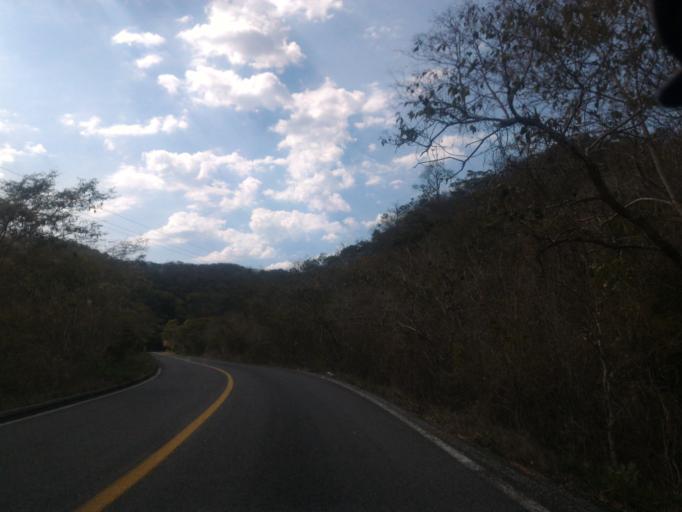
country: MX
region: Michoacan
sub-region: Coalcoman de Vazquez Pallares
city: Coalcoman de Vazquez Pallares
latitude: 18.2843
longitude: -103.3798
